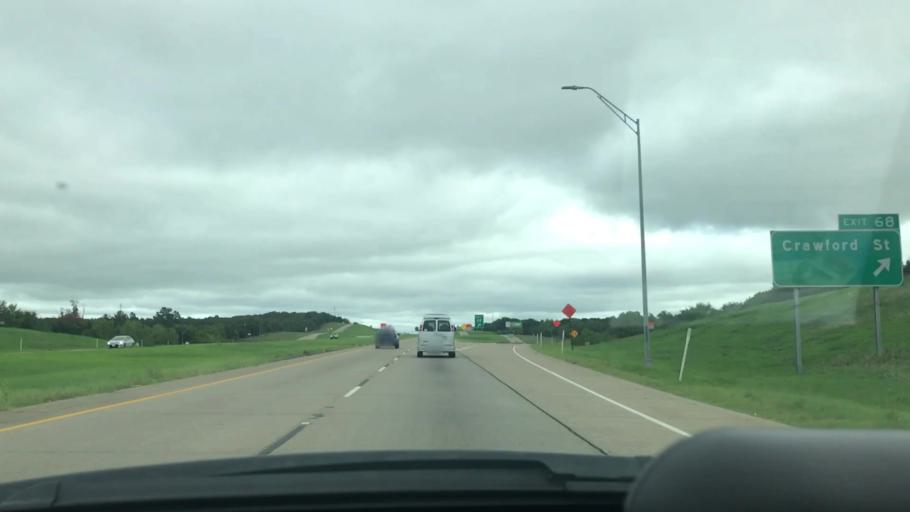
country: US
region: Texas
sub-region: Grayson County
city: Denison
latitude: 33.7436
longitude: -96.5852
